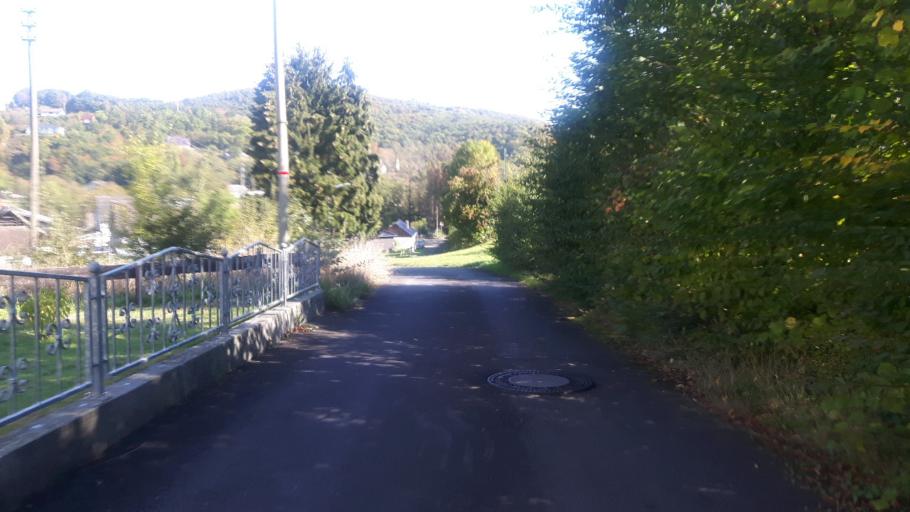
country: DE
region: Rheinland-Pfalz
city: Furthen
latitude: 50.7812
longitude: 7.6690
